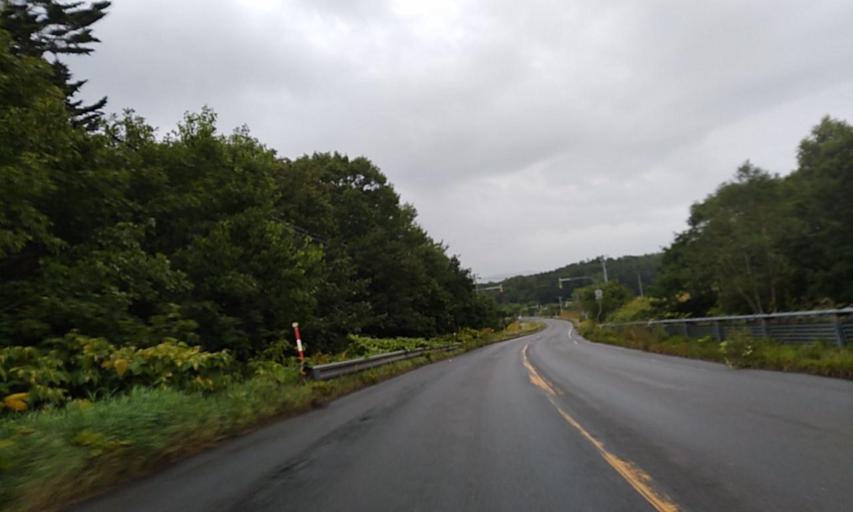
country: JP
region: Hokkaido
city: Mombetsu
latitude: 44.5029
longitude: 143.0746
